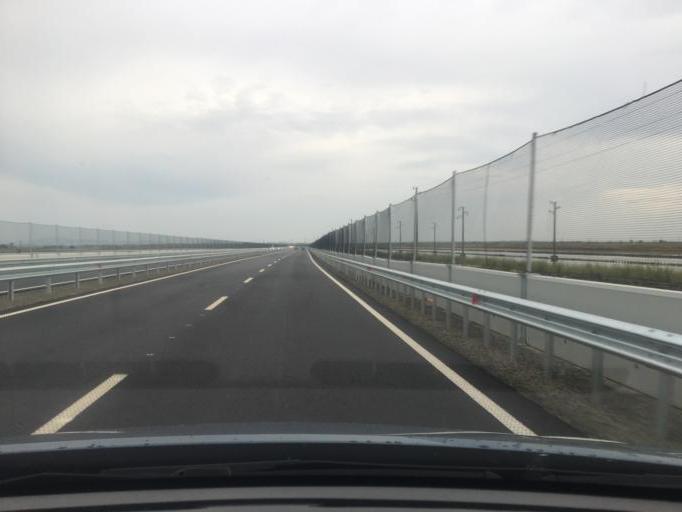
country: BG
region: Burgas
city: Aheloy
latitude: 42.6248
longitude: 27.6298
